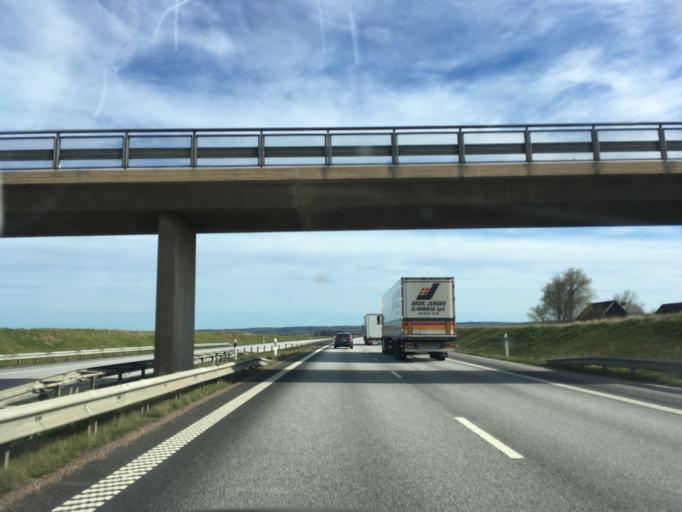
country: SE
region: Skane
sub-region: Angelholms Kommun
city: AEngelholm
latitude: 56.2706
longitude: 12.8943
